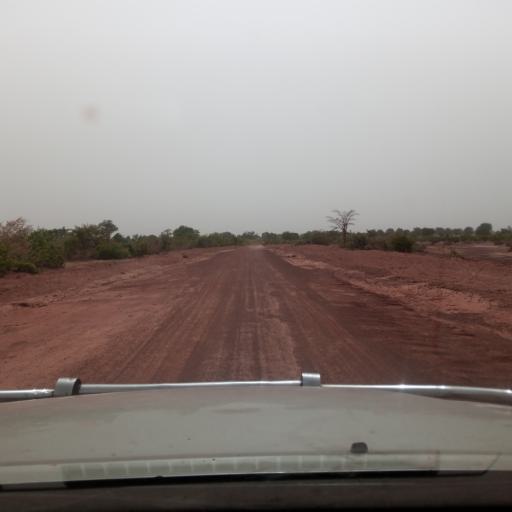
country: ML
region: Koulikoro
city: Banamba
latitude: 13.3425
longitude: -7.5115
